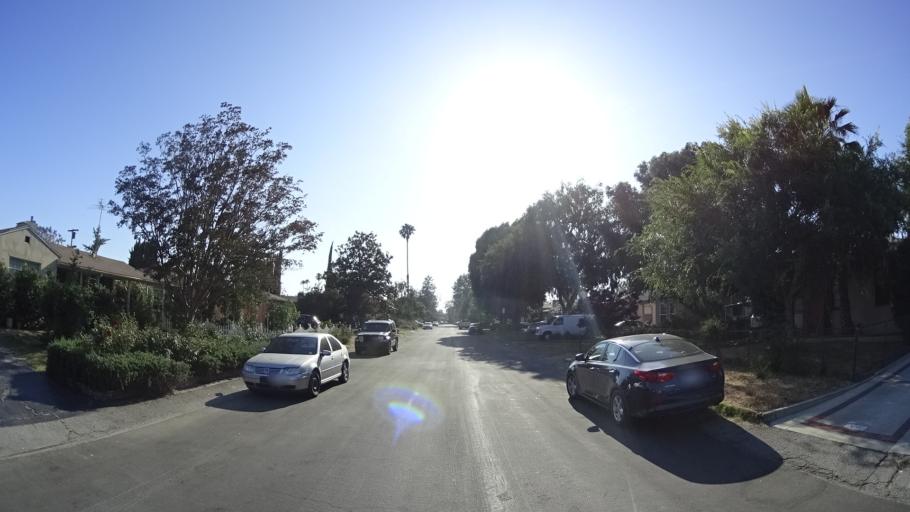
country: US
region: California
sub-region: Los Angeles County
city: Van Nuys
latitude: 34.1749
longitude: -118.4445
